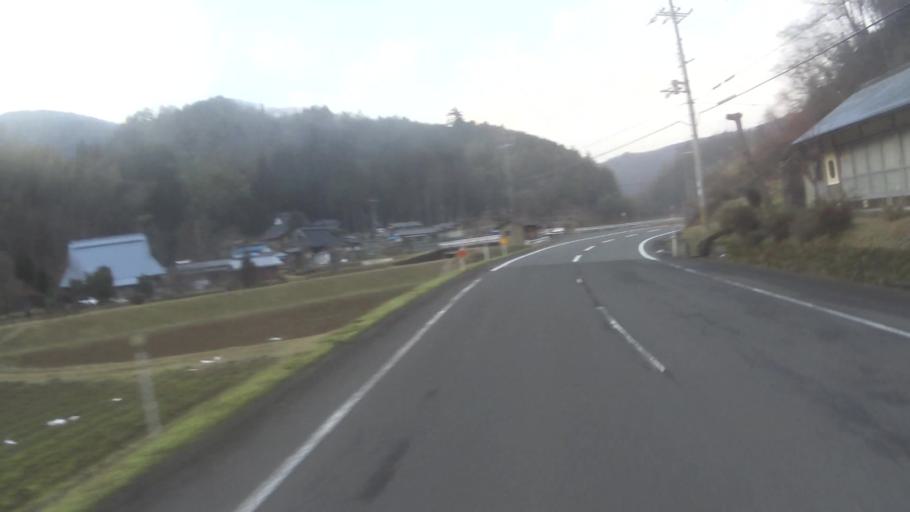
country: JP
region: Kyoto
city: Maizuru
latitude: 35.3999
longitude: 135.4627
